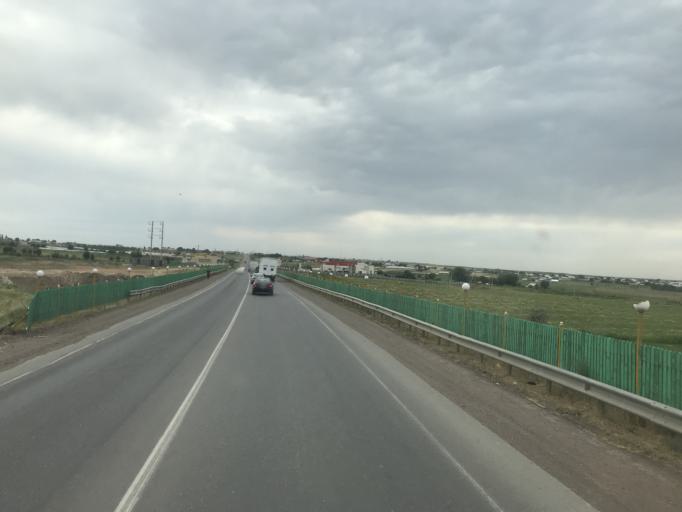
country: KZ
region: Ongtustik Qazaqstan
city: Saryaghash
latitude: 41.4572
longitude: 69.1393
